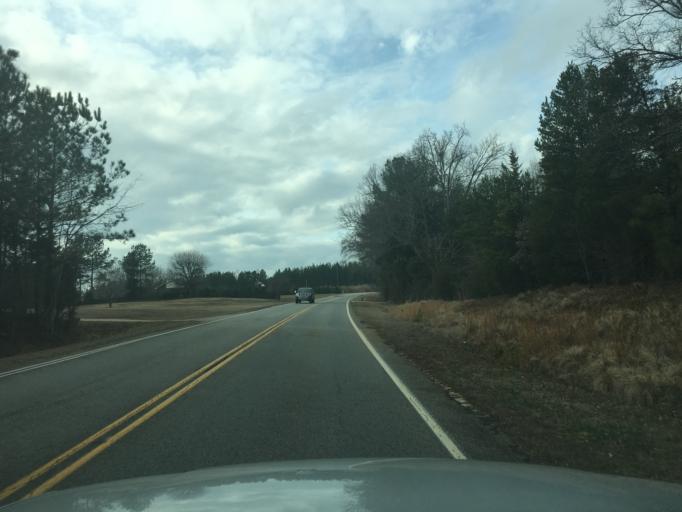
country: US
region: South Carolina
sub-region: Abbeville County
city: Due West
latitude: 34.2892
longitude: -82.4444
